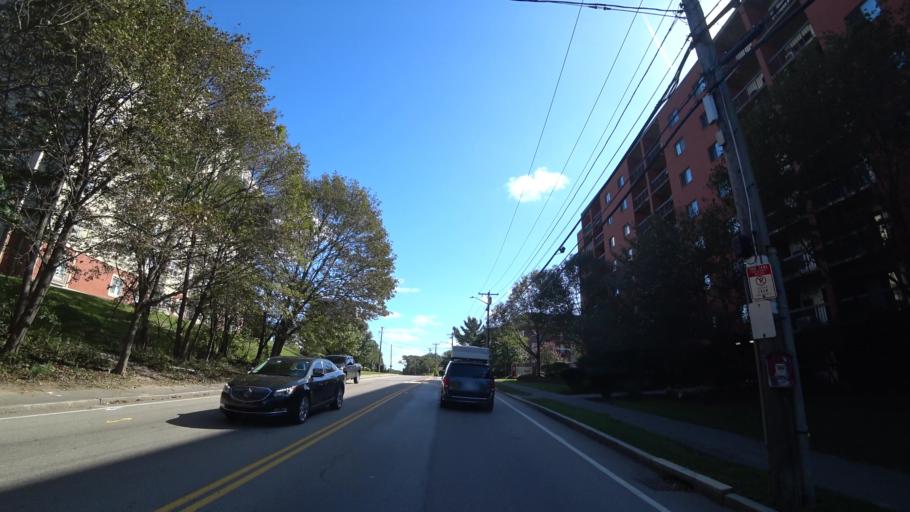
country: US
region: Massachusetts
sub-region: Norfolk County
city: Quincy
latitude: 42.2491
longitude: -71.0221
